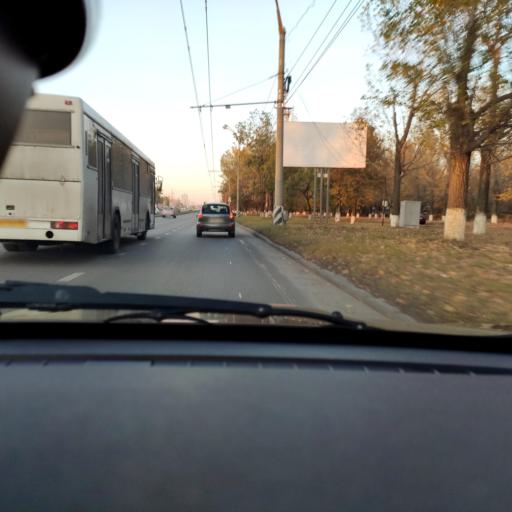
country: RU
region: Samara
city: Tol'yatti
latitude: 53.5257
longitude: 49.2606
